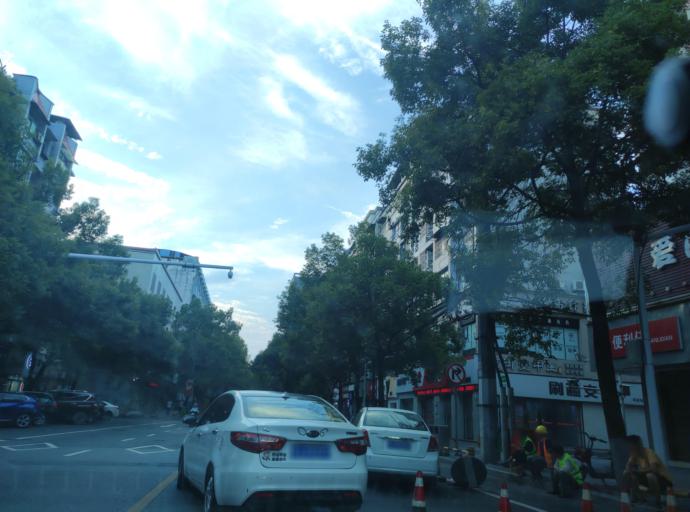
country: CN
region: Jiangxi Sheng
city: Pingxiang
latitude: 27.6309
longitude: 113.8490
